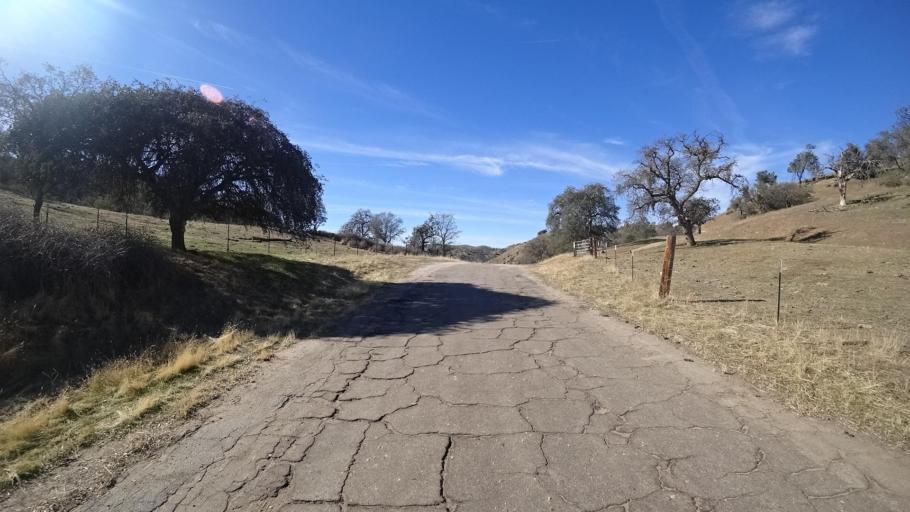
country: US
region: California
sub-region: Kern County
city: Arvin
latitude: 35.4406
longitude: -118.7222
